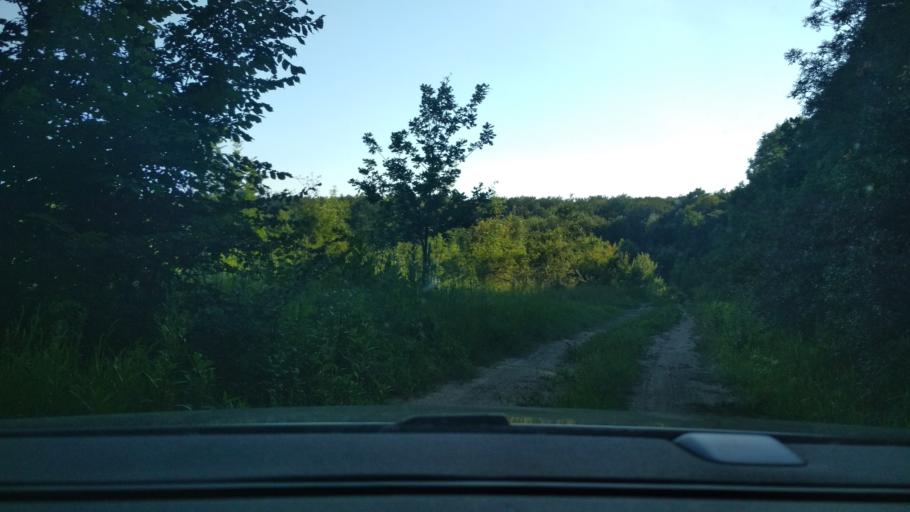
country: MD
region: Stinga Nistrului
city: Bucovat
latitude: 47.0811
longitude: 28.3710
